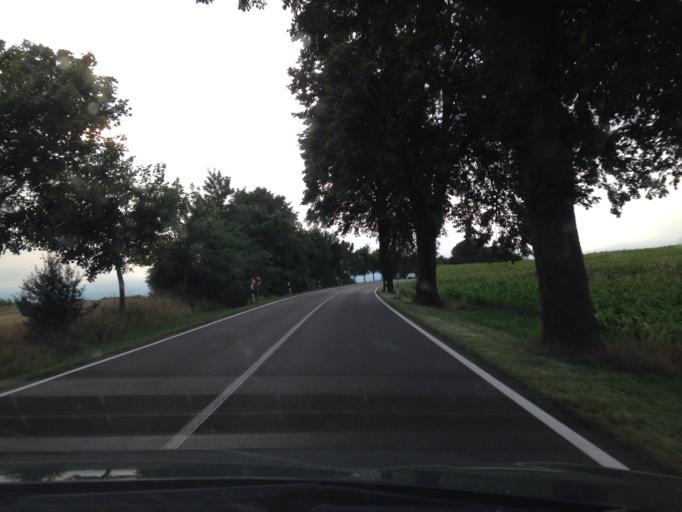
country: DE
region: Mecklenburg-Vorpommern
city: Loitz
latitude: 53.3643
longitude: 13.3830
